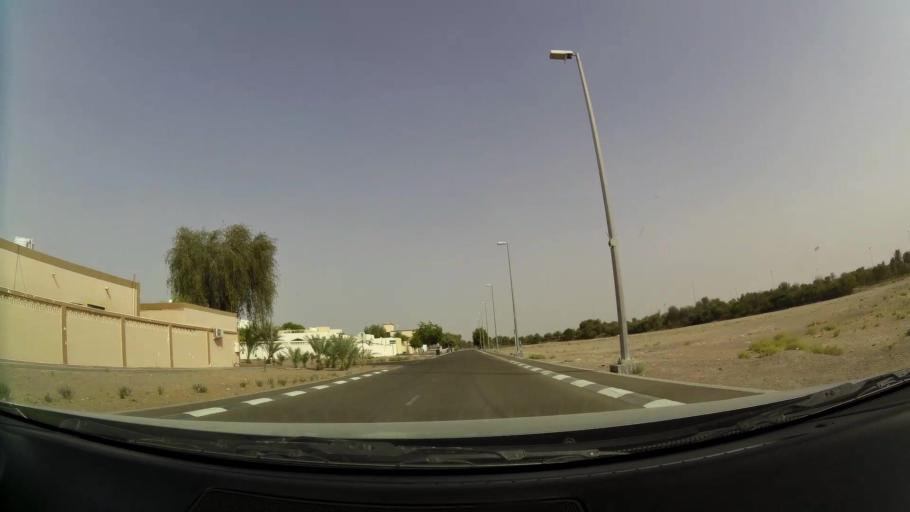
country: AE
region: Abu Dhabi
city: Al Ain
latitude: 24.2037
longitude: 55.5854
